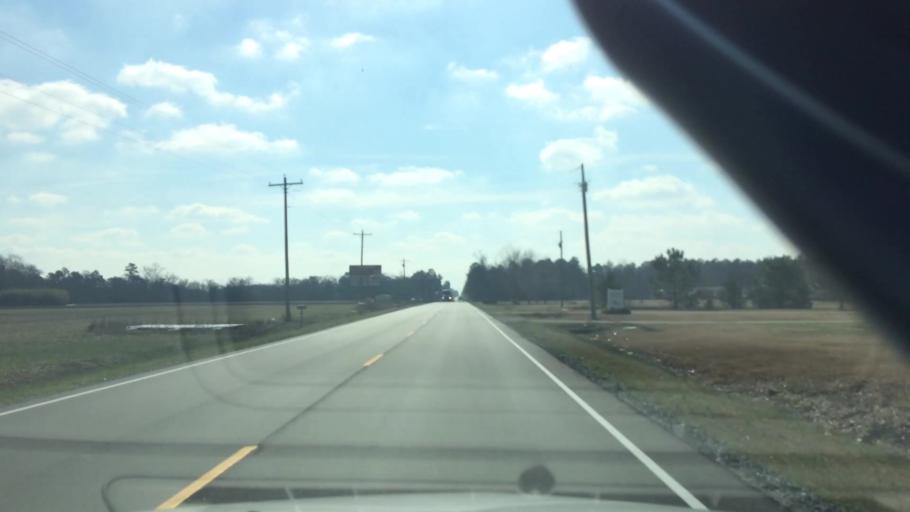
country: US
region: North Carolina
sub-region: Duplin County
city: Beulaville
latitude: 35.0205
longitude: -77.7505
